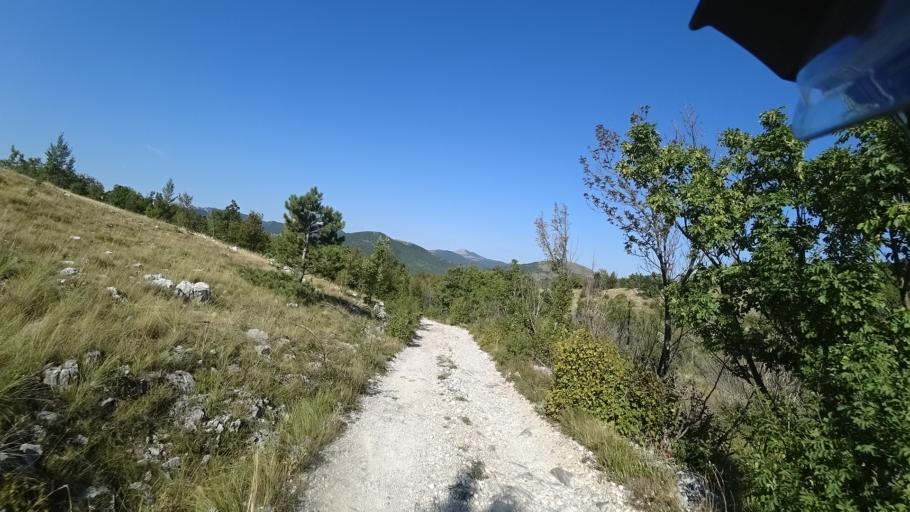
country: HR
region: Sibensko-Kniniska
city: Knin
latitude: 44.2288
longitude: 16.0879
